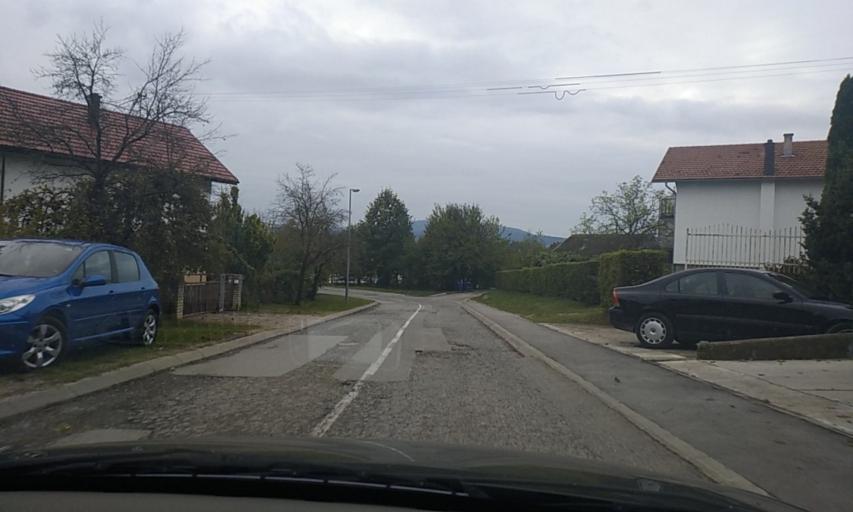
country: BA
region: Republika Srpska
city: Prnjavor
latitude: 44.8591
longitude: 17.6787
